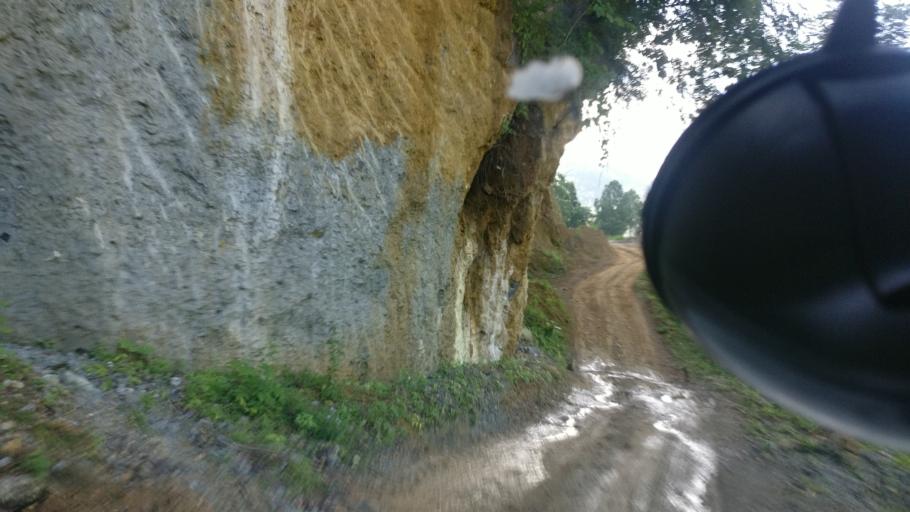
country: NP
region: Western Region
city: Baglung
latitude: 28.1590
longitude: 83.6542
